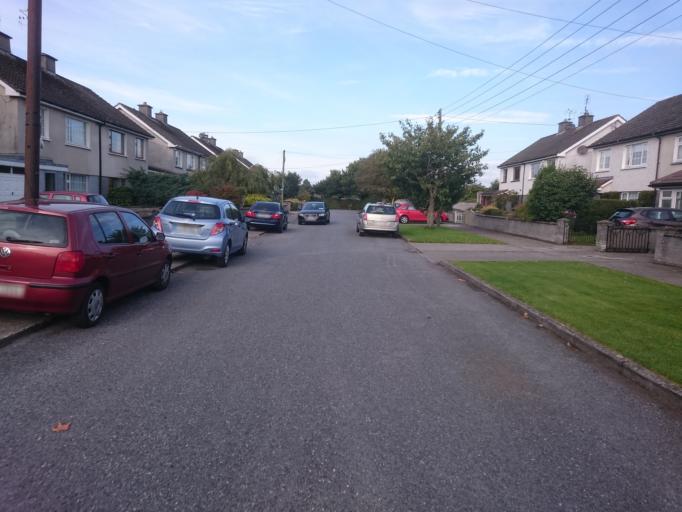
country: IE
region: Leinster
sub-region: Kilkenny
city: Kilkenny
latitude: 52.6511
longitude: -7.2316
